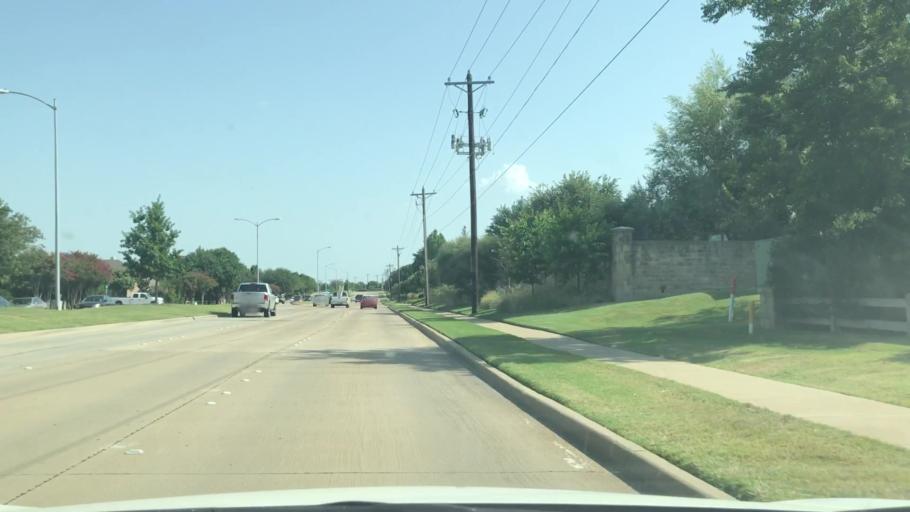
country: US
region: Texas
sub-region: Collin County
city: Allen
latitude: 33.1085
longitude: -96.7509
